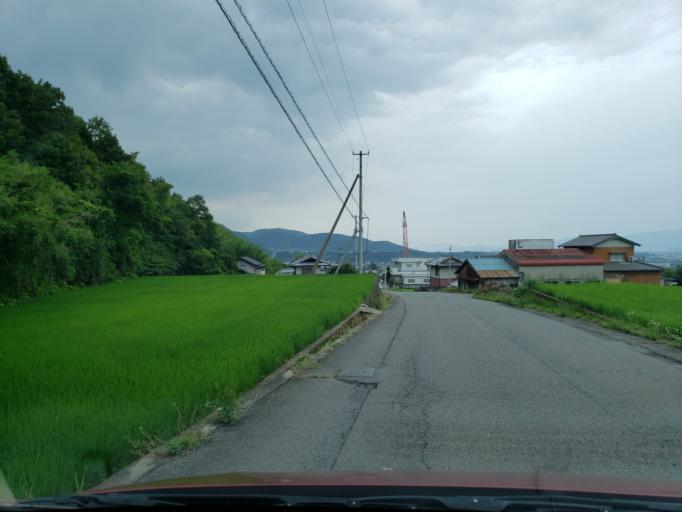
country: JP
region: Tokushima
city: Kamojimacho-jogejima
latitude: 34.1059
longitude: 134.2564
